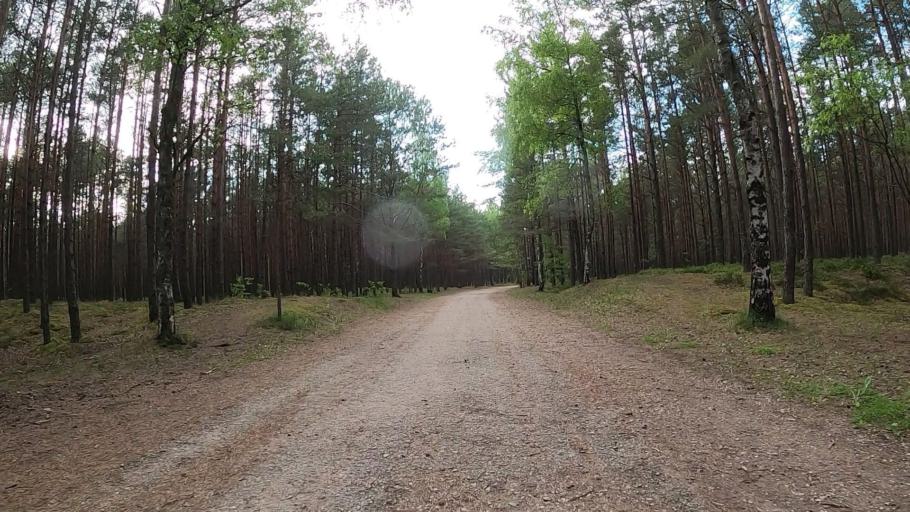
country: LV
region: Riga
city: Jaunciems
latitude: 57.0897
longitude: 24.1504
